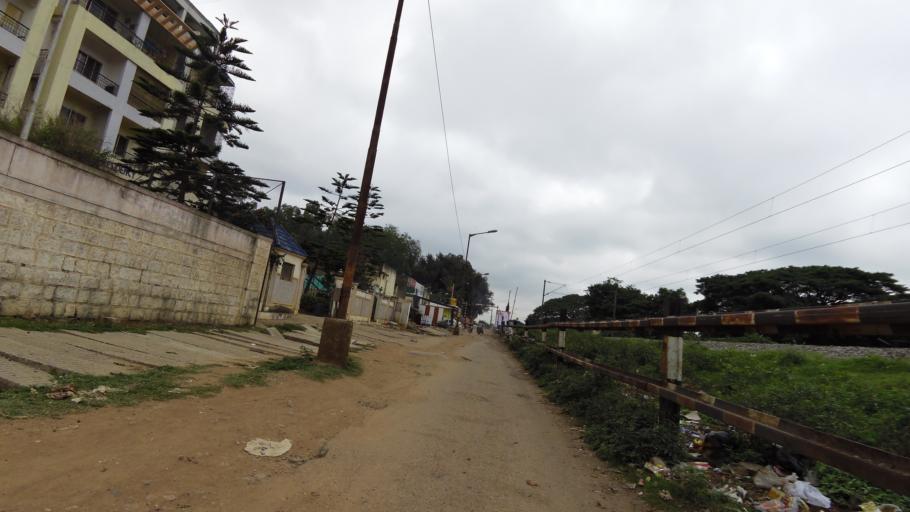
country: IN
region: Karnataka
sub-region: Bangalore Urban
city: Bangalore
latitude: 12.9943
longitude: 77.6310
